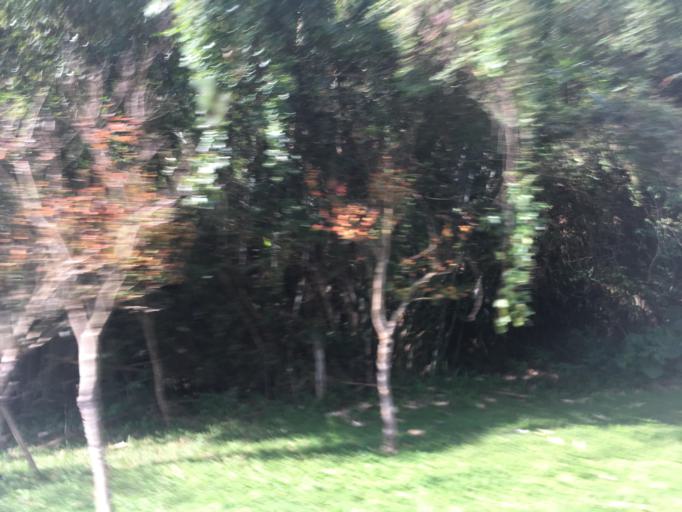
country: TW
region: Taiwan
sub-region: Yilan
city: Yilan
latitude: 24.6699
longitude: 121.6038
